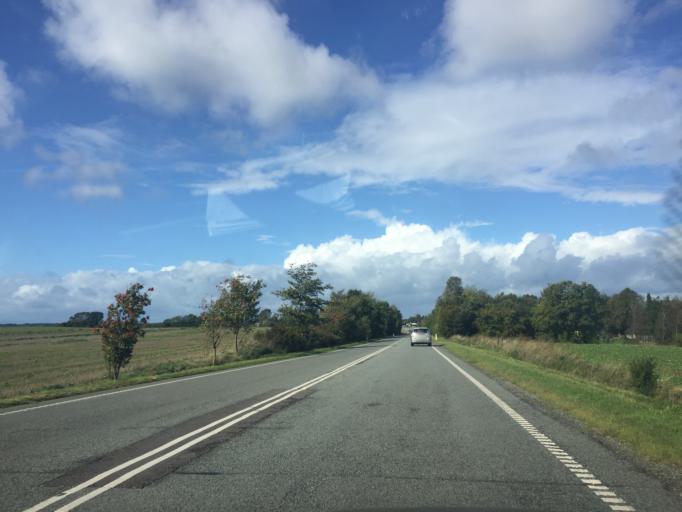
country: DK
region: Capital Region
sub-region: Gribskov Kommune
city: Helsinge
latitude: 56.0322
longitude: 12.1629
